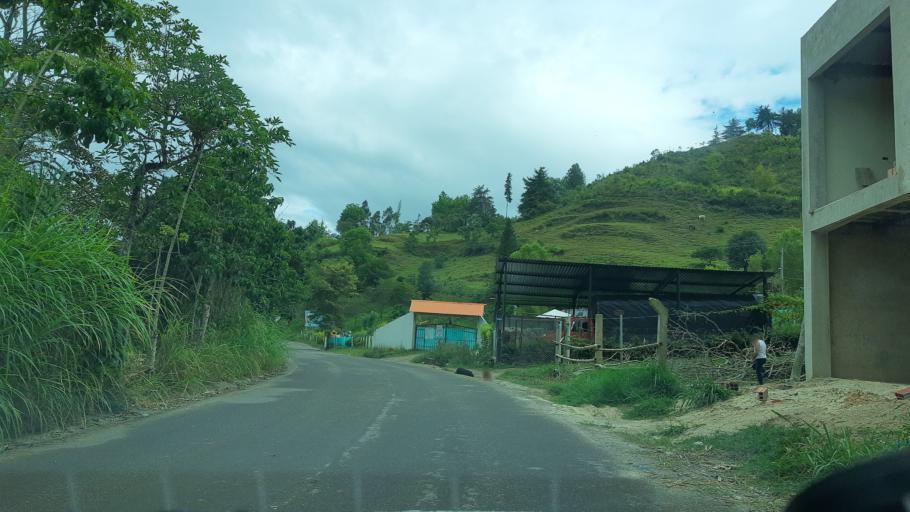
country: CO
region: Cundinamarca
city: Tenza
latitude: 5.0855
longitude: -73.4373
